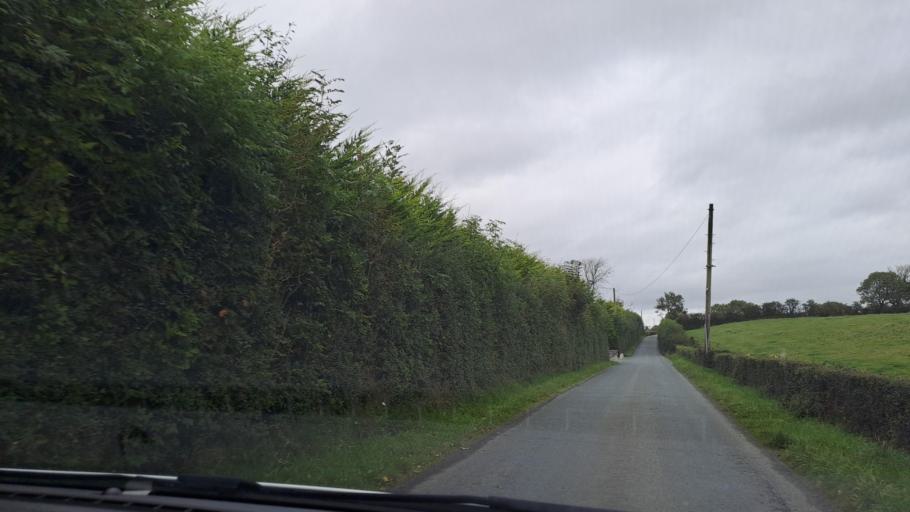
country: IE
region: Ulster
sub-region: An Cabhan
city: Kingscourt
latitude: 54.0075
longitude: -6.8564
